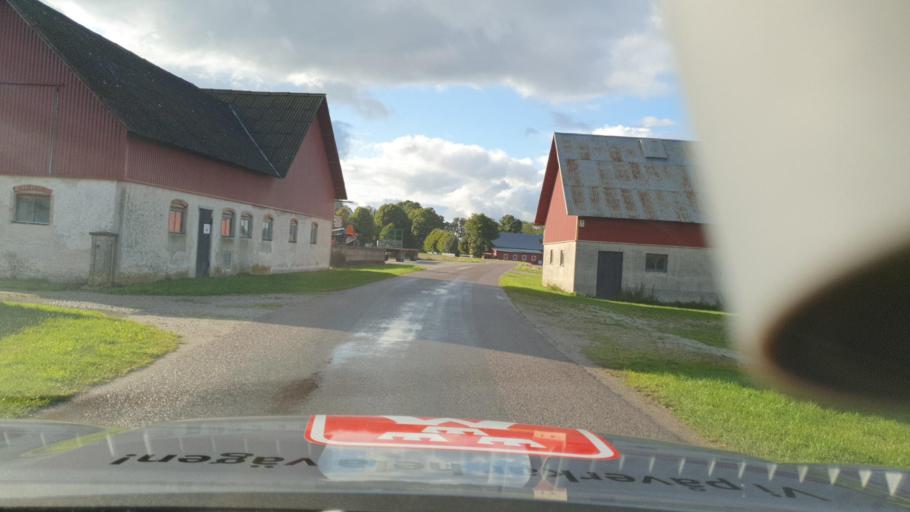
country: SE
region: Gotland
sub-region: Gotland
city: Hemse
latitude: 57.1853
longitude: 18.2667
